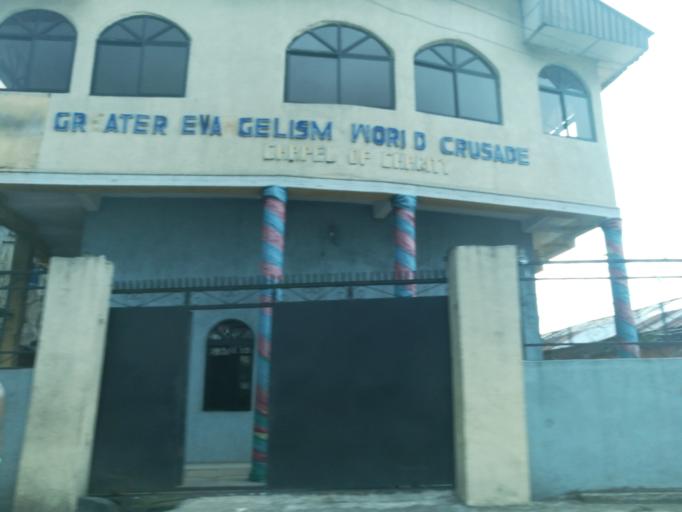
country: NG
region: Rivers
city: Port Harcourt
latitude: 4.7939
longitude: 6.9846
